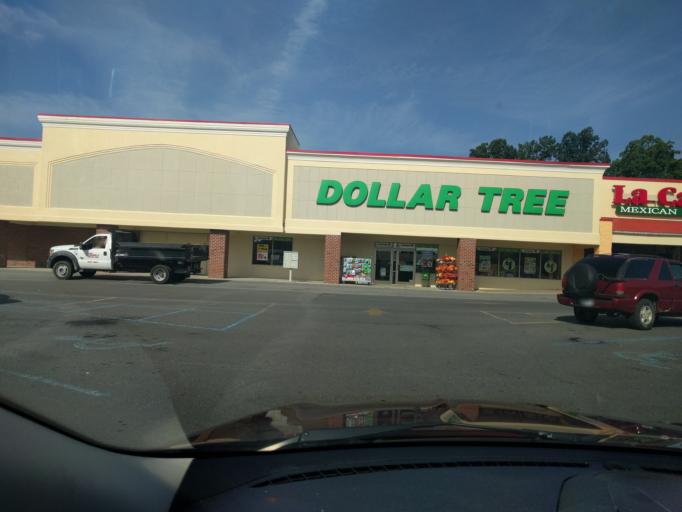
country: US
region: West Virginia
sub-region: Nicholas County
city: Summersville
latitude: 38.2978
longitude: -80.8350
